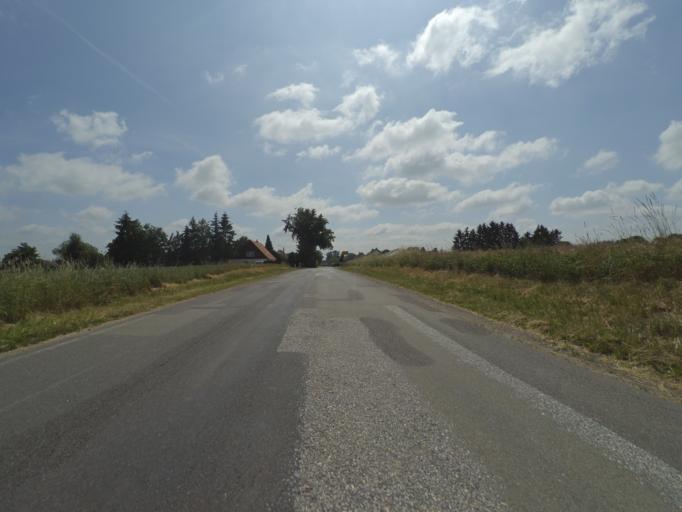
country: DE
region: Mecklenburg-Vorpommern
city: Siggelkow
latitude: 53.4260
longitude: 11.9704
